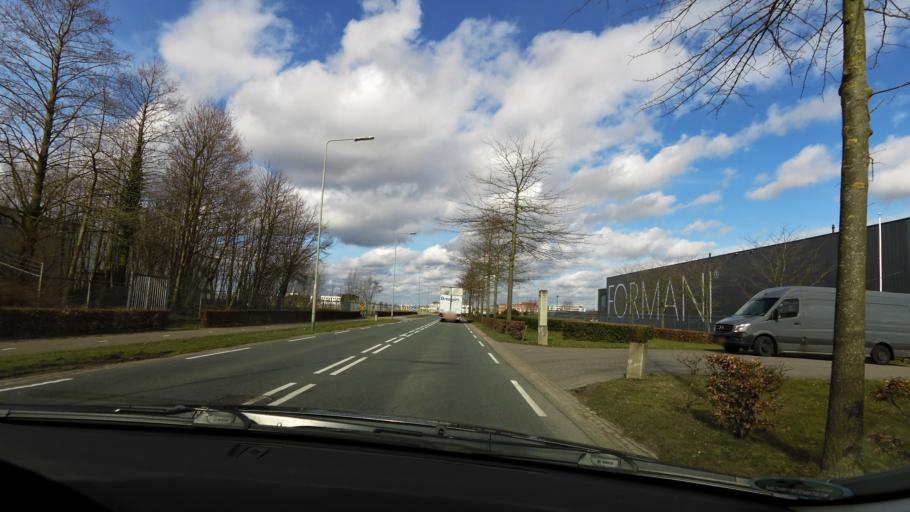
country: NL
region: Limburg
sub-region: Gemeente Beek
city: Beek
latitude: 50.9220
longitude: 5.7859
